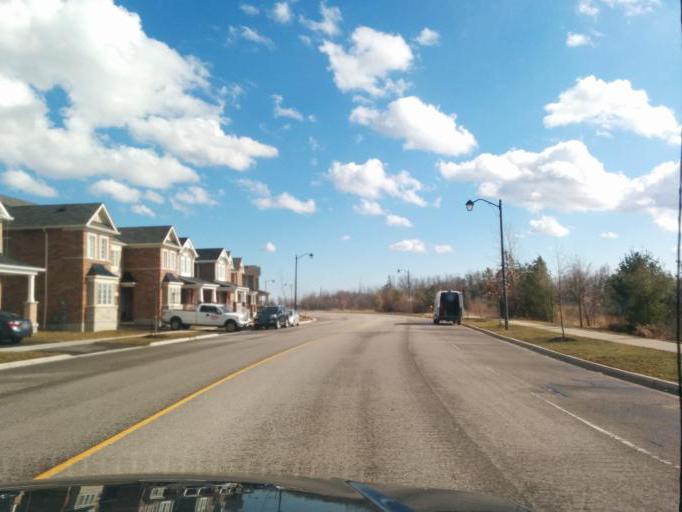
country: CA
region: Ontario
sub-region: Halton
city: Milton
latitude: 43.5024
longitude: -79.8470
